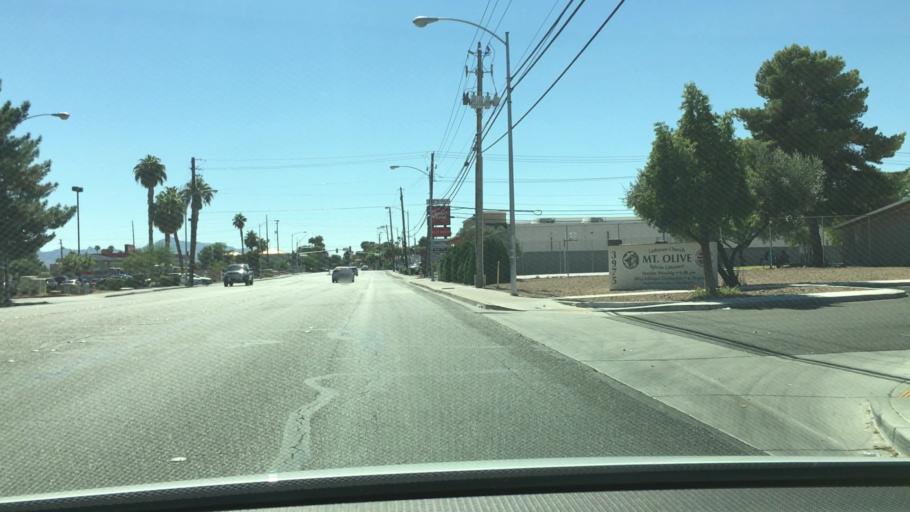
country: US
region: Nevada
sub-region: Clark County
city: Winchester
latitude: 36.1179
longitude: -115.0921
